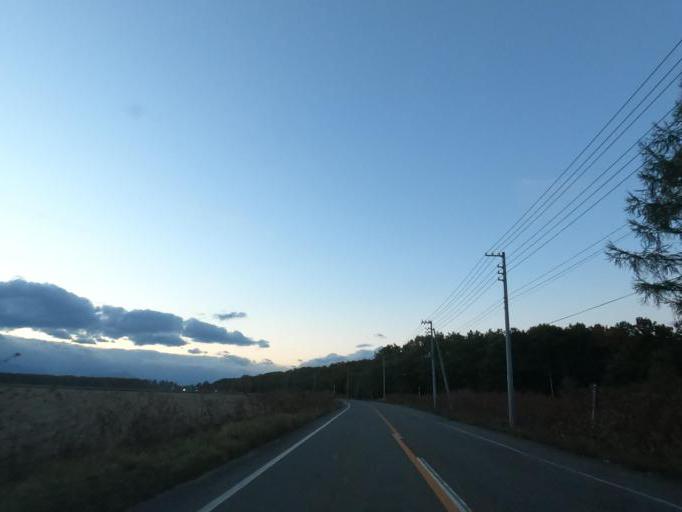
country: JP
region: Hokkaido
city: Obihiro
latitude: 42.6747
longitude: 143.1665
